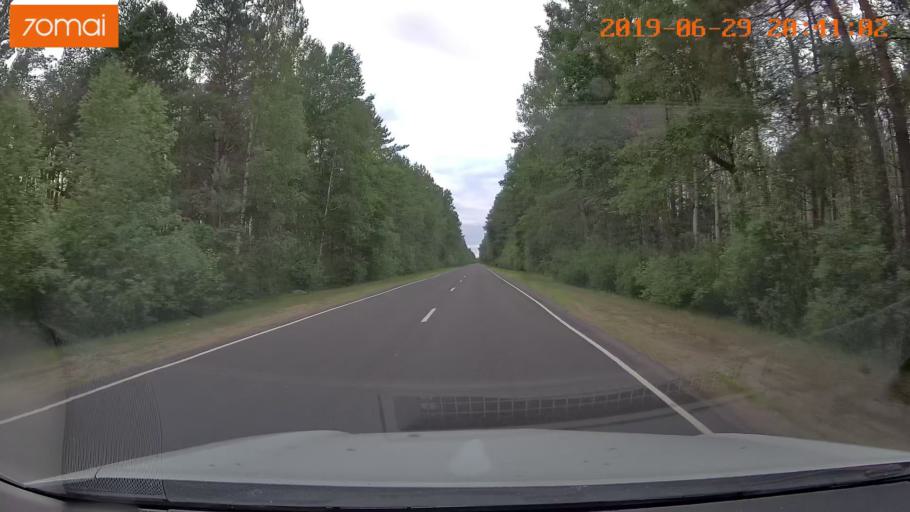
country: BY
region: Brest
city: Hantsavichy
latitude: 52.5810
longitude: 26.3445
